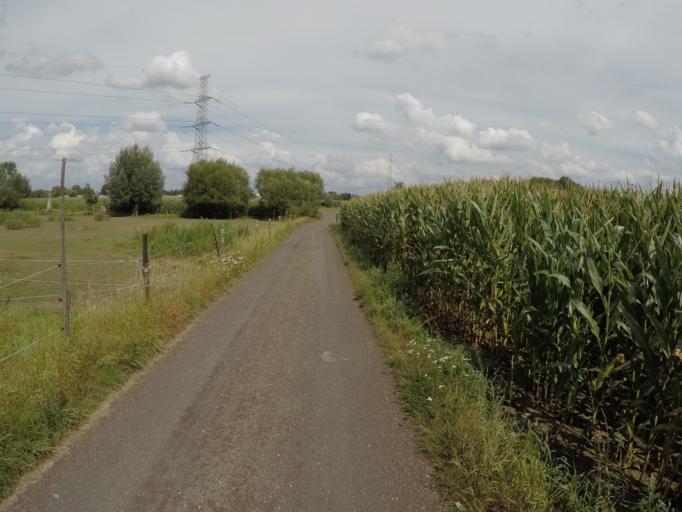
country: BE
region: Flanders
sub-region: Provincie Antwerpen
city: Ranst
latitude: 51.1639
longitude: 4.5569
